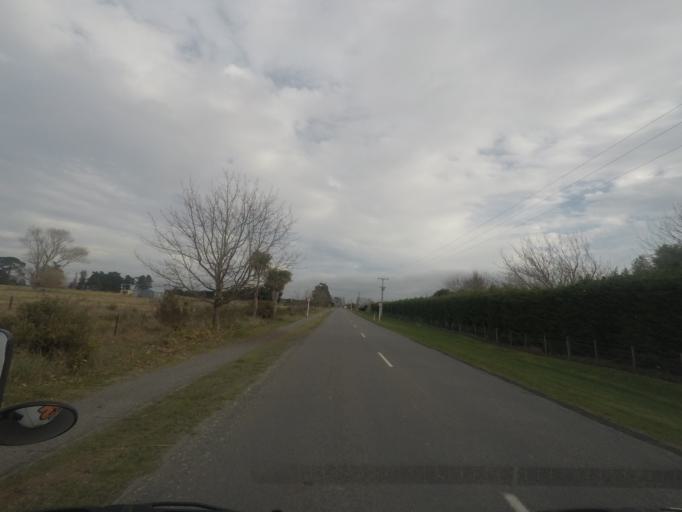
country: NZ
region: Canterbury
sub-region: Waimakariri District
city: Woodend
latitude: -43.2880
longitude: 172.7074
